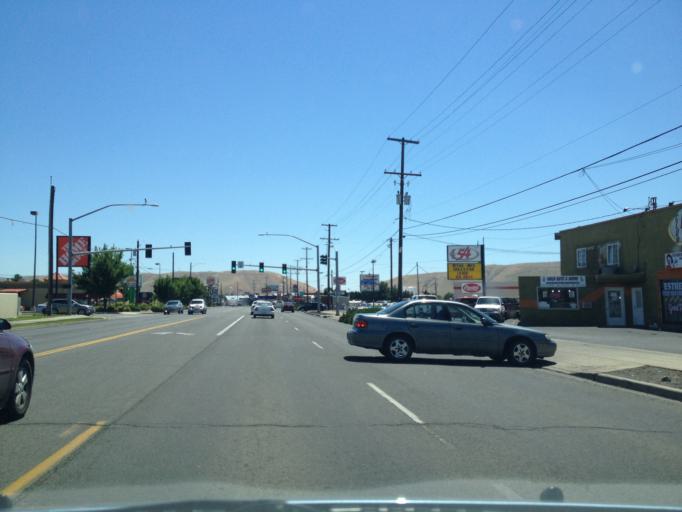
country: US
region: Washington
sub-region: Yakima County
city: Union Gap
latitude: 46.5733
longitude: -120.4893
